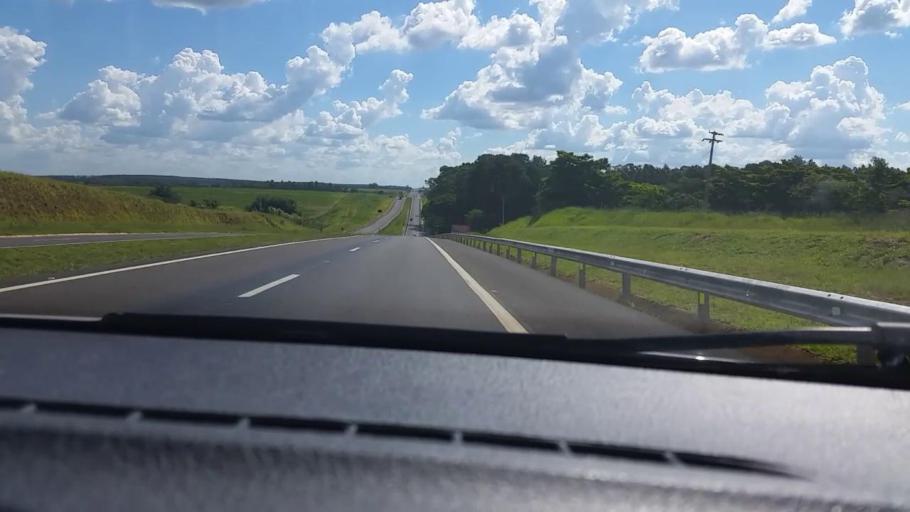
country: BR
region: Sao Paulo
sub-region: Bauru
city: Bauru
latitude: -22.4425
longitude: -49.1514
